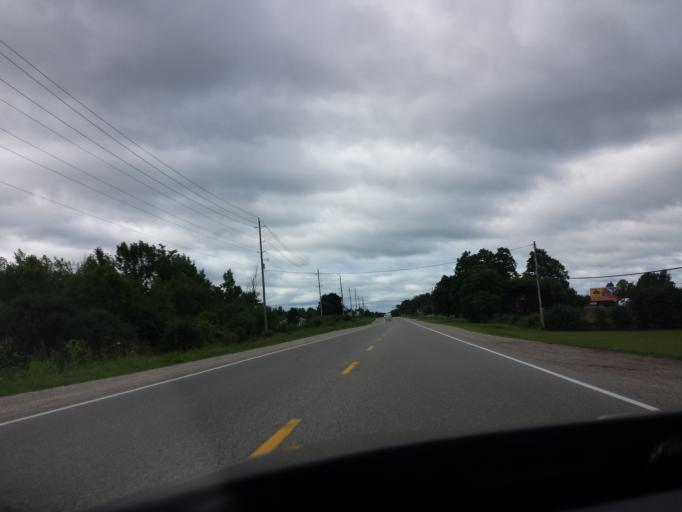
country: CA
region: Ontario
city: Perth
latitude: 44.9243
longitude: -76.2501
